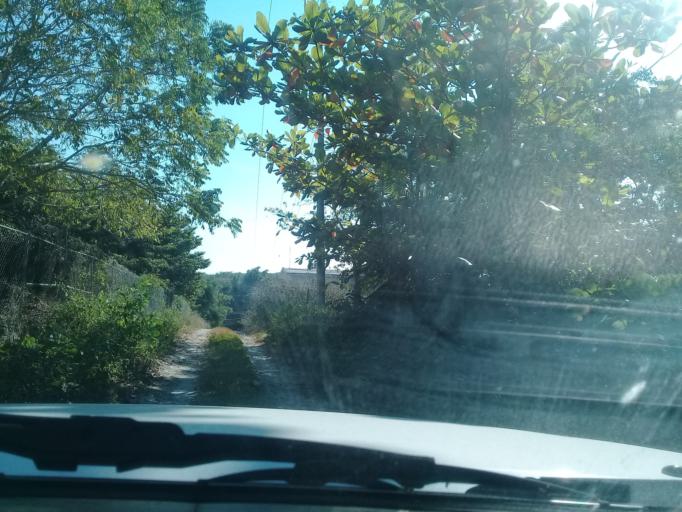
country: MX
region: Veracruz
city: Rinconada
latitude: 19.4018
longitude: -96.5604
